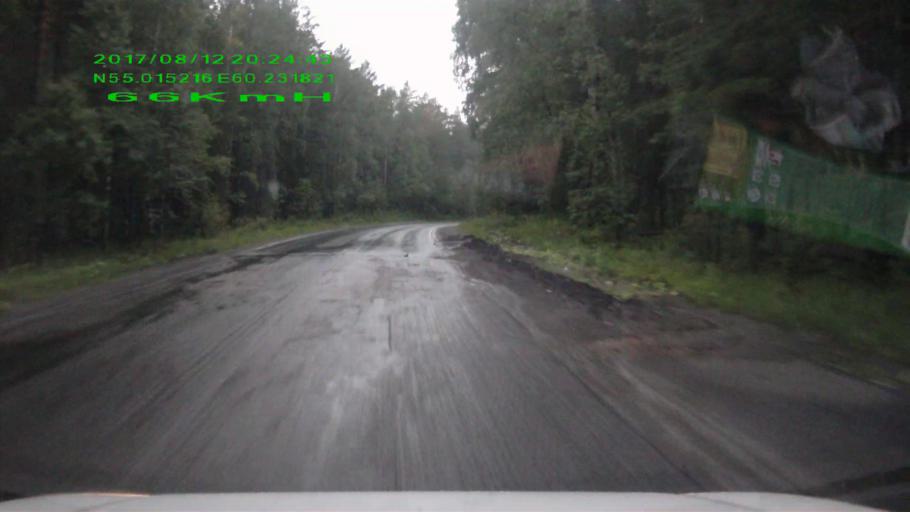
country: RU
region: Chelyabinsk
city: Miass
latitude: 55.0150
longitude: 60.2316
